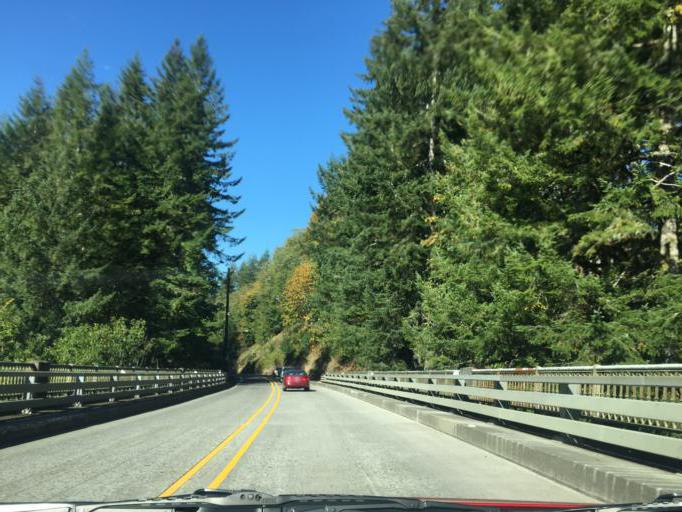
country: US
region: Oregon
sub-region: Columbia County
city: Vernonia
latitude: 45.8415
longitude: -123.5181
